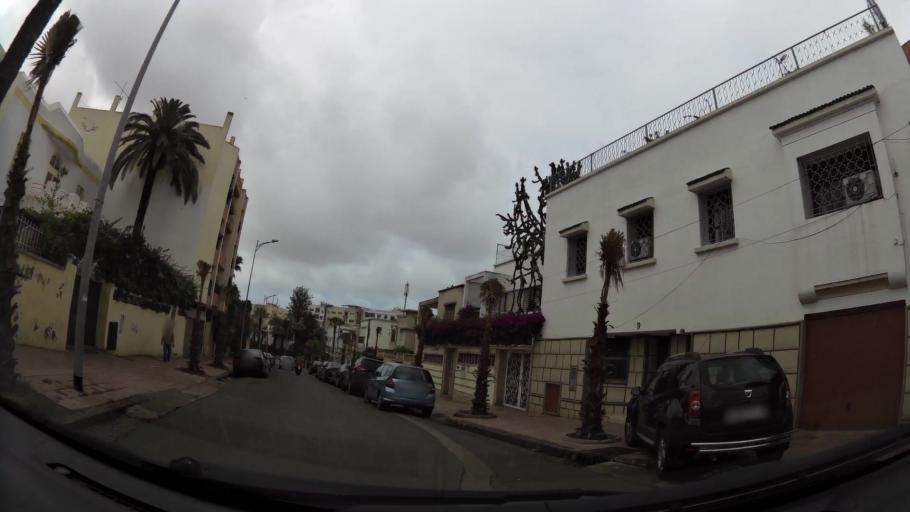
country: MA
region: Grand Casablanca
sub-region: Casablanca
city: Casablanca
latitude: 33.5824
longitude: -7.6098
